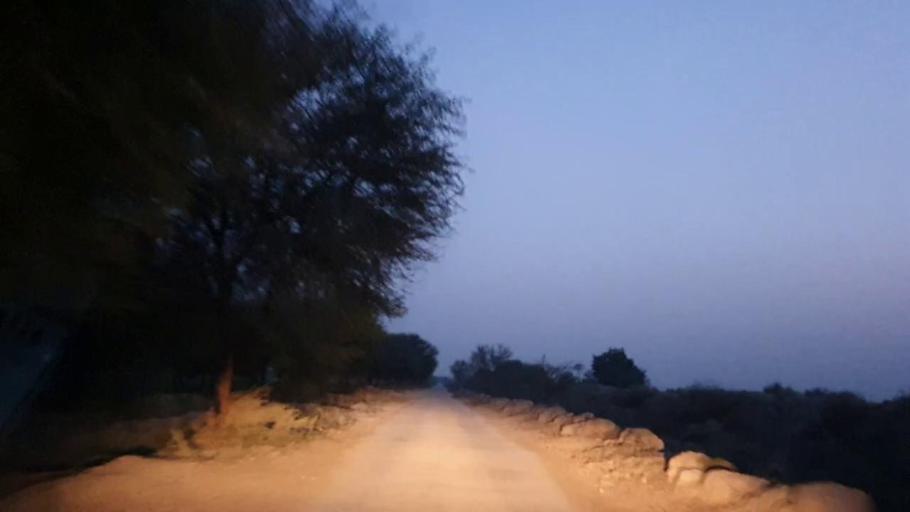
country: PK
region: Sindh
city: Tando Ghulam Ali
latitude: 25.0902
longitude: 68.9178
